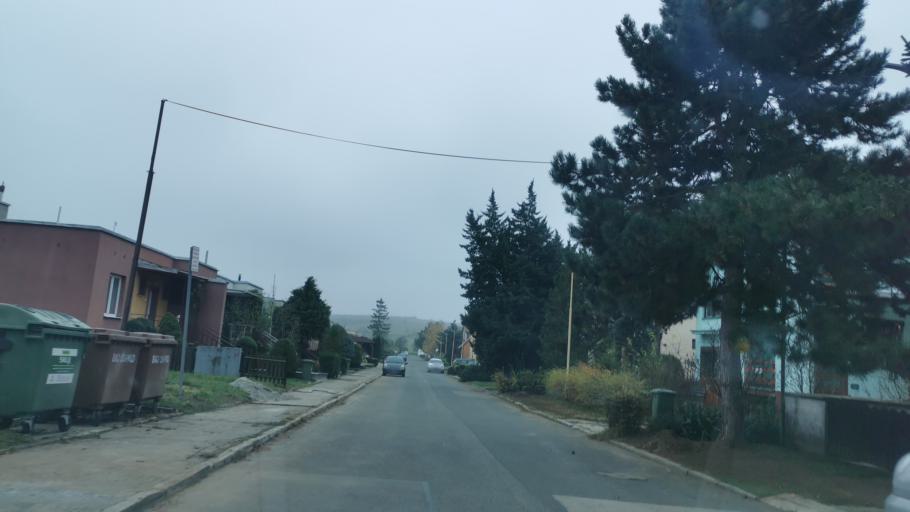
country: SK
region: Trnavsky
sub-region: Okres Skalica
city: Holic
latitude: 48.8135
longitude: 17.1705
